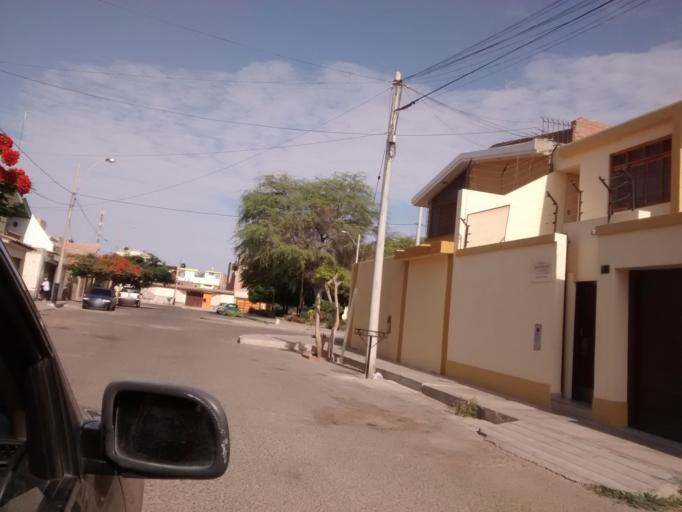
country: PE
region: Piura
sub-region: Provincia de Piura
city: Piura
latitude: -5.1713
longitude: -80.6284
